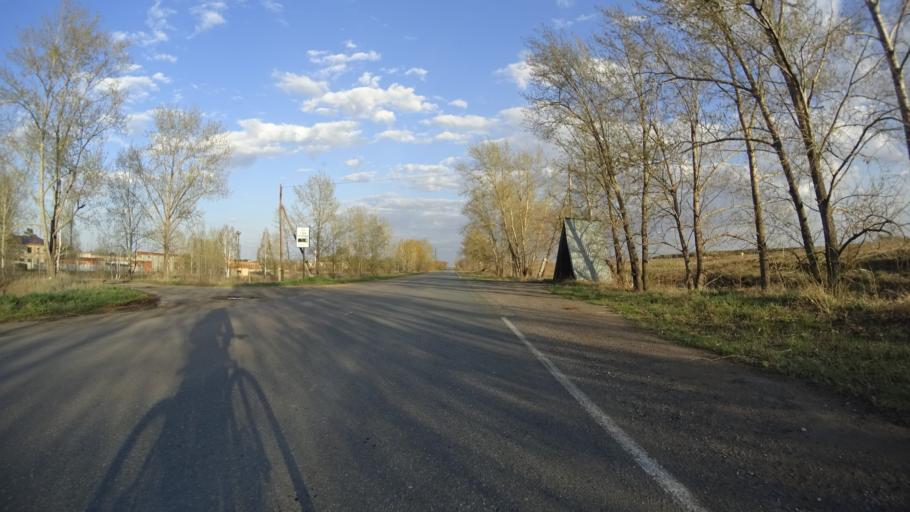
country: RU
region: Chelyabinsk
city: Troitsk
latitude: 54.0563
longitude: 61.5854
